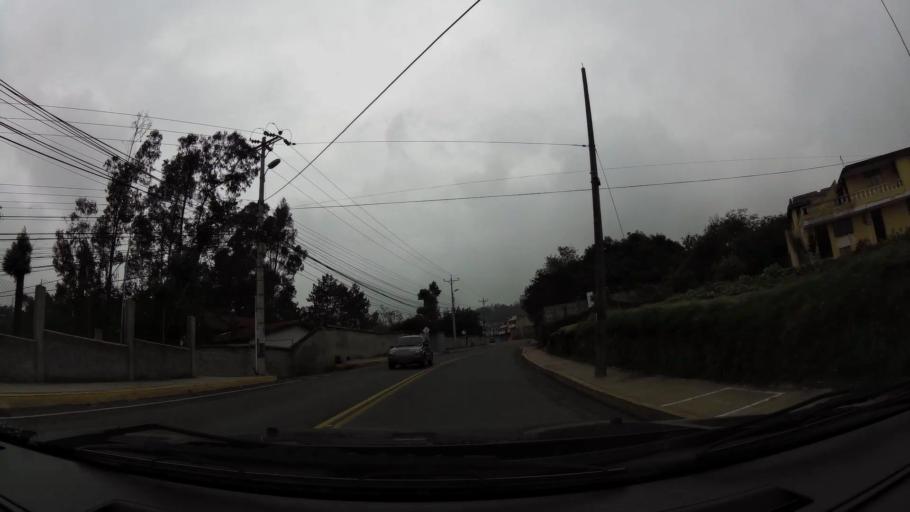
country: EC
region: Pichincha
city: Quito
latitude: -0.2628
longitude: -78.4827
